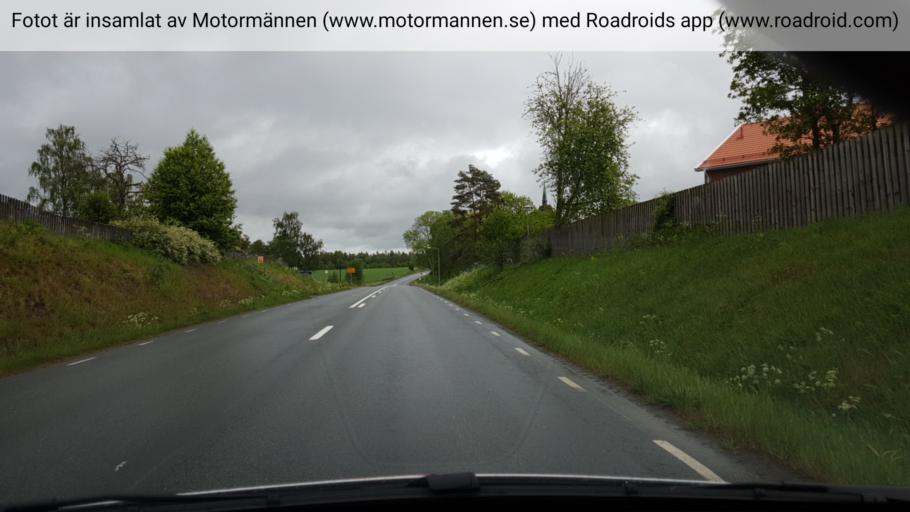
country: SE
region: Joenkoeping
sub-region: Aneby Kommun
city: Hestra
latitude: 57.7770
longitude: 14.5565
